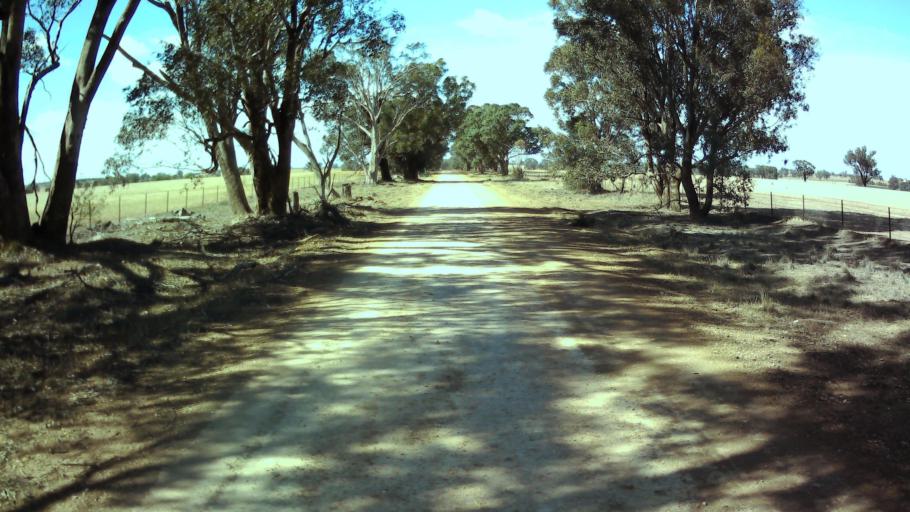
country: AU
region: New South Wales
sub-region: Weddin
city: Grenfell
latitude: -34.0532
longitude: 148.3135
